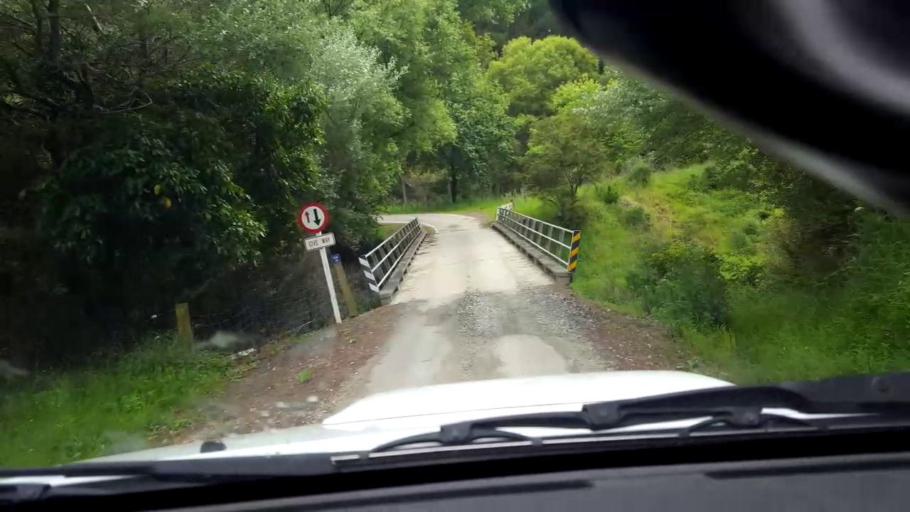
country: NZ
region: Gisborne
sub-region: Gisborne District
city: Gisborne
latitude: -38.3819
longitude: 177.6280
